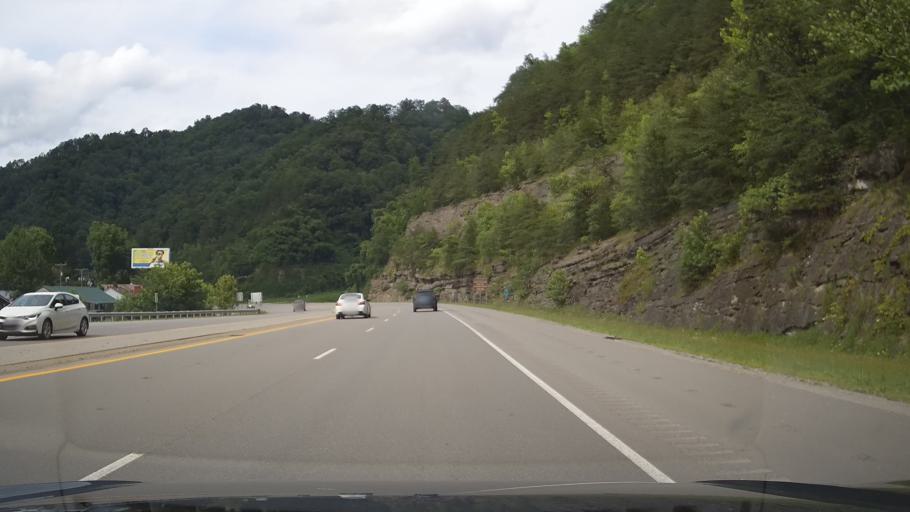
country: US
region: Kentucky
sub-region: Pike County
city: Pikeville
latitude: 37.4422
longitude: -82.5060
